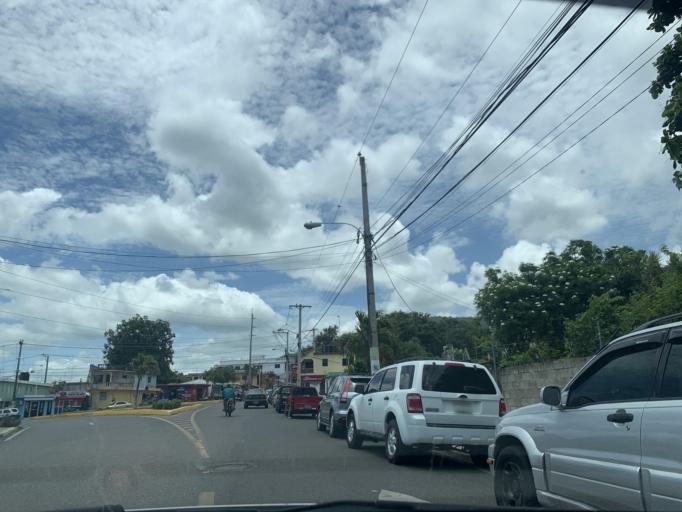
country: DO
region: Puerto Plata
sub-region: Puerto Plata
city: Puerto Plata
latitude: 19.7863
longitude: -70.6919
